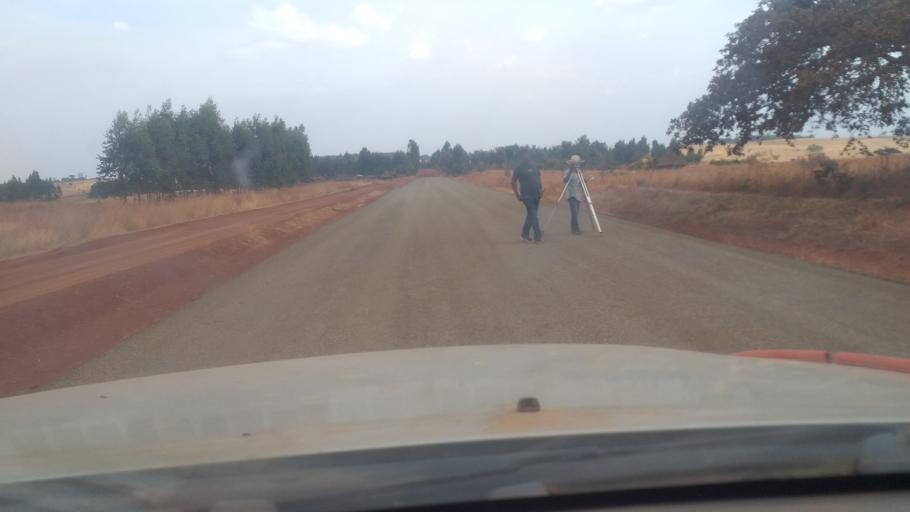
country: ET
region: Binshangul Gumuz
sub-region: Asosa
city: Asosa
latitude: 10.0796
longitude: 34.6219
